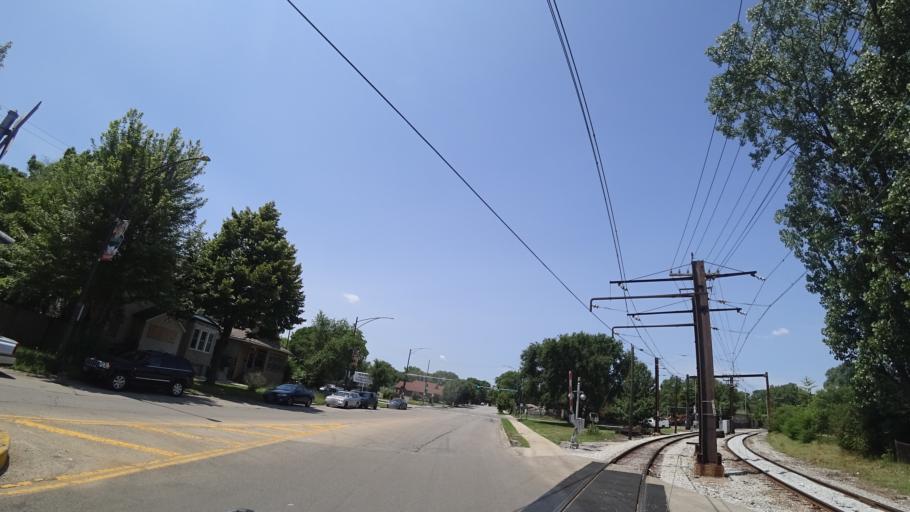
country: US
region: Illinois
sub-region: Cook County
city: Chicago
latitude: 41.7661
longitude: -87.5901
